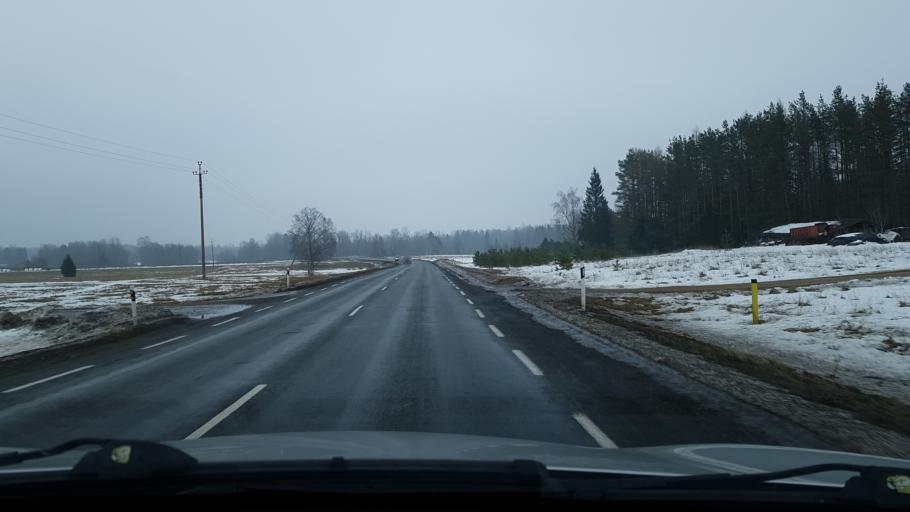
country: EE
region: Viljandimaa
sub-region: Viiratsi vald
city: Viiratsi
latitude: 58.2485
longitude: 25.7751
